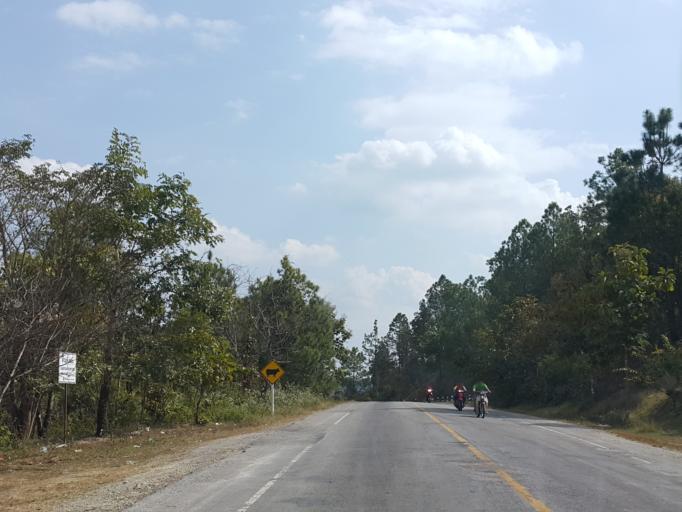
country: TH
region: Chiang Mai
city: Om Koi
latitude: 17.8192
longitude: 98.3661
